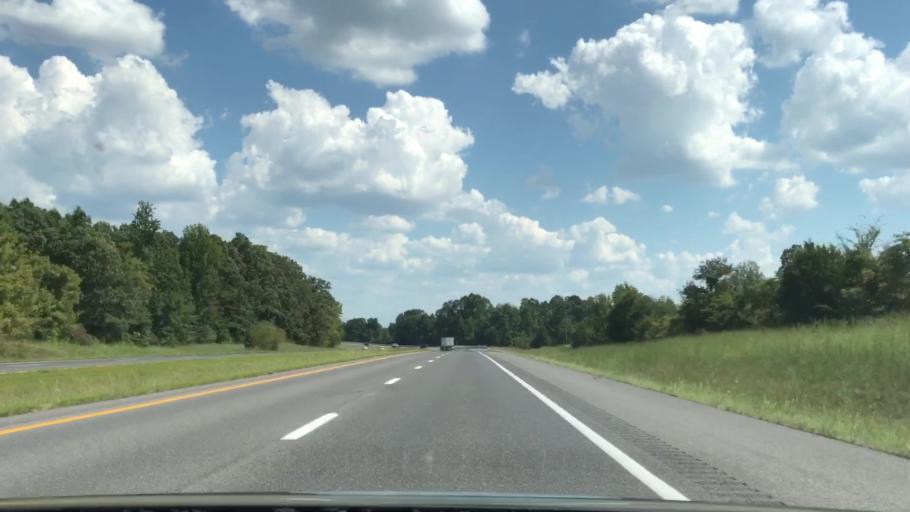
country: US
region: Kentucky
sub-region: Lyon County
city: Eddyville
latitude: 37.1070
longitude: -87.9904
